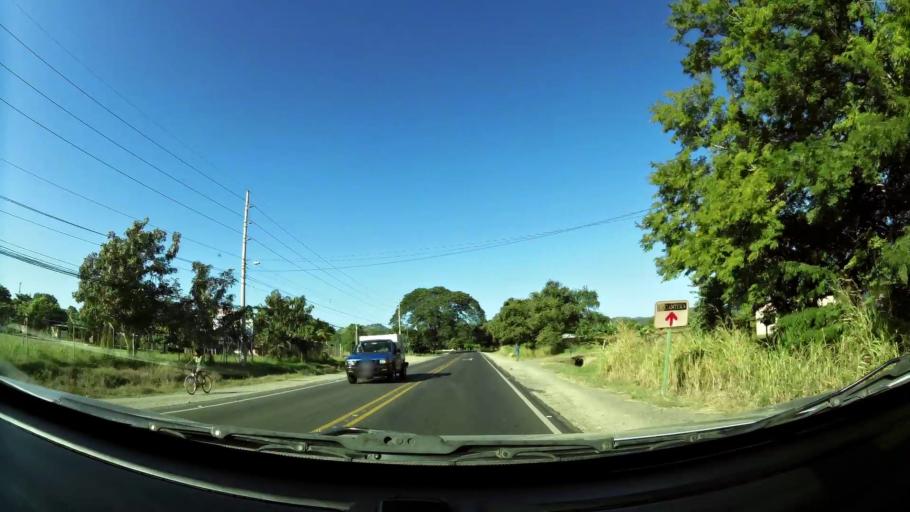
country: CR
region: Guanacaste
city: Belen
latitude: 10.4117
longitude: -85.5830
